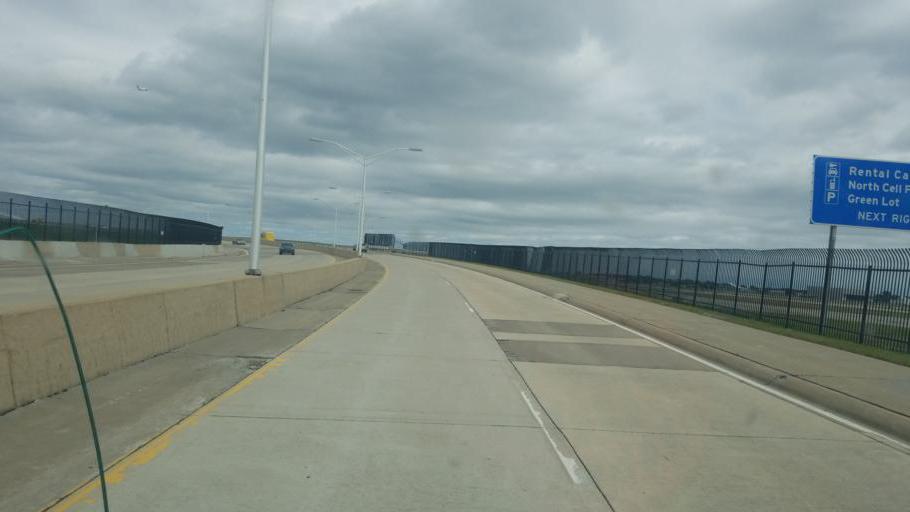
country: US
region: Michigan
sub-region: Wayne County
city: Romulus
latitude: 42.2227
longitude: -83.3430
